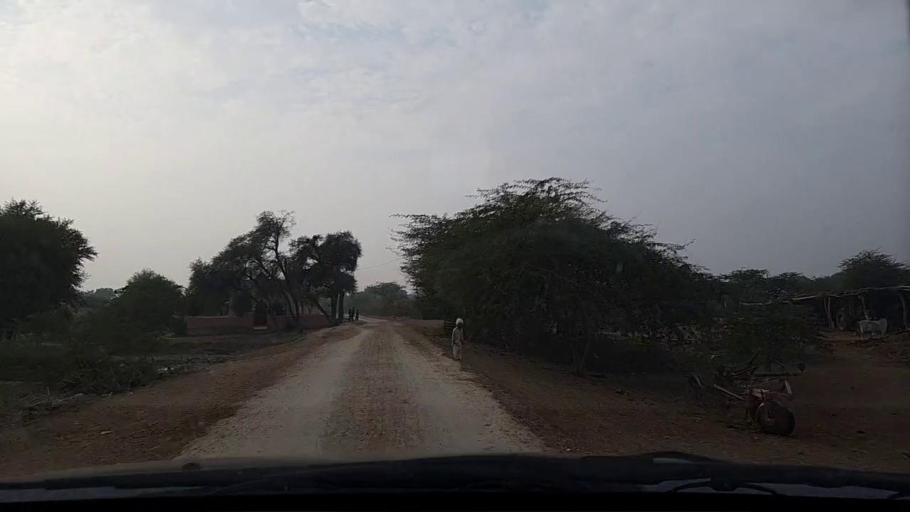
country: PK
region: Sindh
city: Pithoro
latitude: 25.7101
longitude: 69.3888
